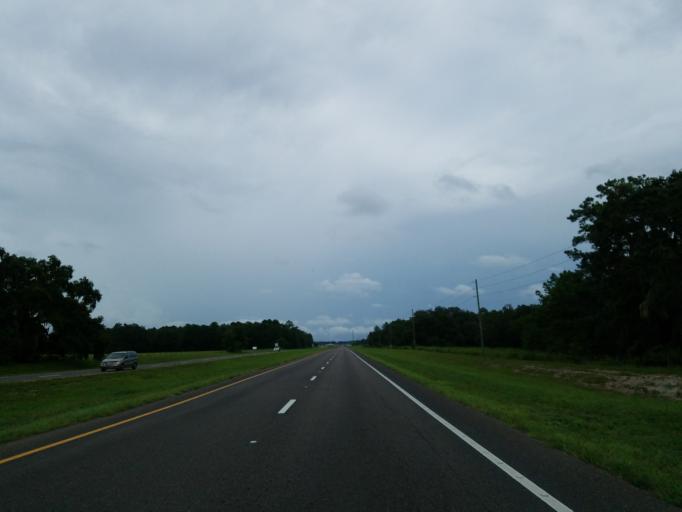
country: US
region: Florida
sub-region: Sumter County
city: Wildwood
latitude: 28.8787
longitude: -82.1161
